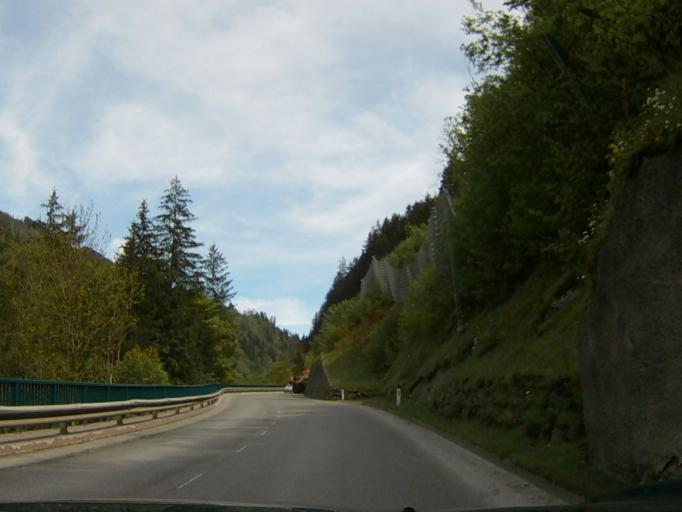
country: AT
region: Tyrol
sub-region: Politischer Bezirk Schwaz
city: Hainzenberg
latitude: 47.2251
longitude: 11.8916
